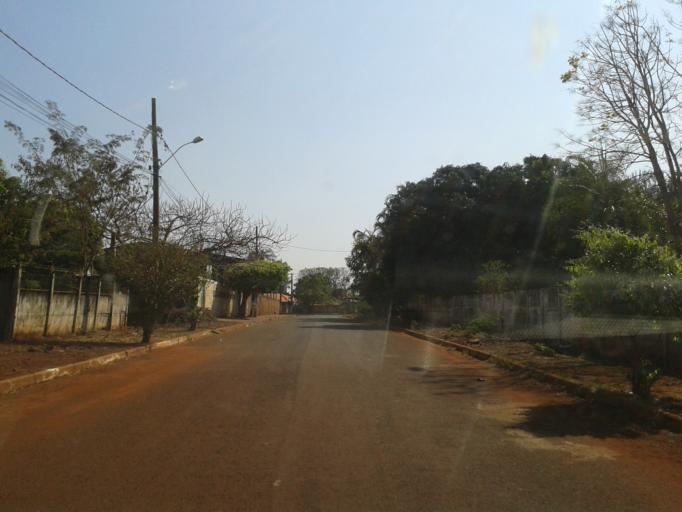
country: BR
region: Minas Gerais
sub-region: Ituiutaba
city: Ituiutaba
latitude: -18.9585
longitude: -49.4775
